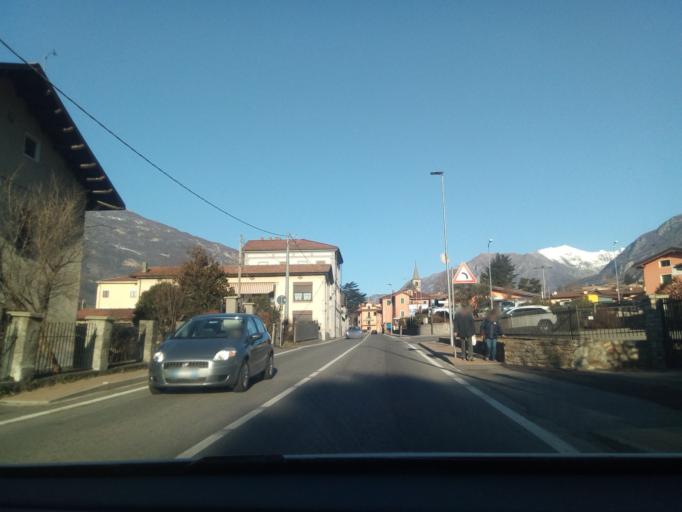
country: IT
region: Piedmont
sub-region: Provincia di Torino
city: Settimo Vittone
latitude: 45.5453
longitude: 7.8345
